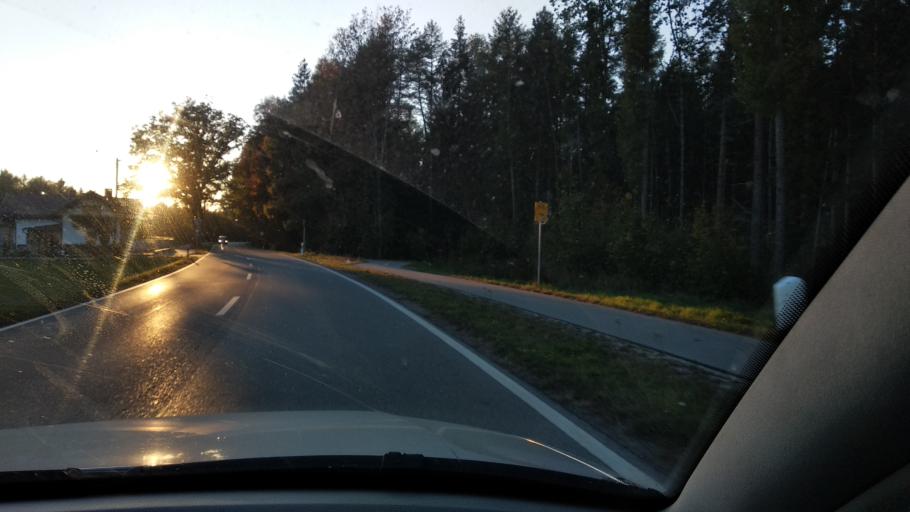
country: DE
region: Bavaria
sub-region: Upper Bavaria
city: Egmating
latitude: 48.0148
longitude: 11.7720
